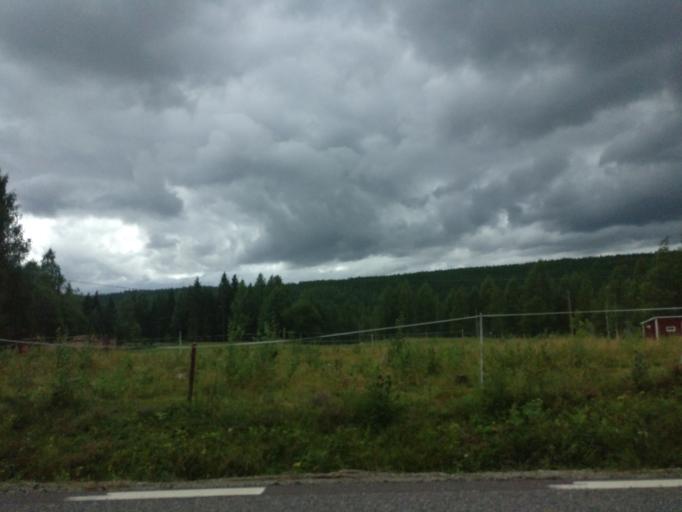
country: SE
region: Vaermland
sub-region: Torsby Kommun
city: Torsby
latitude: 60.7713
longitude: 12.7543
